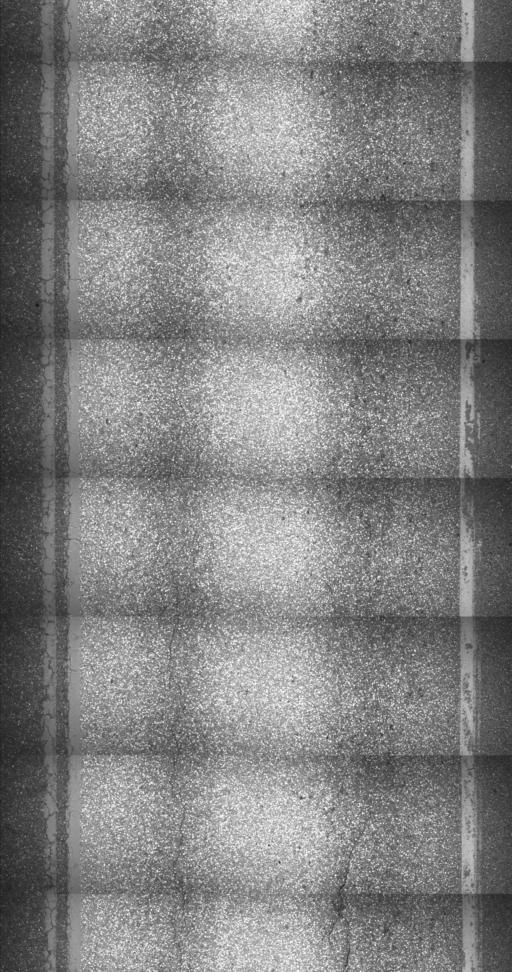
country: US
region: Vermont
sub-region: Franklin County
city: Enosburg Falls
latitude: 44.7957
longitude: -72.8823
